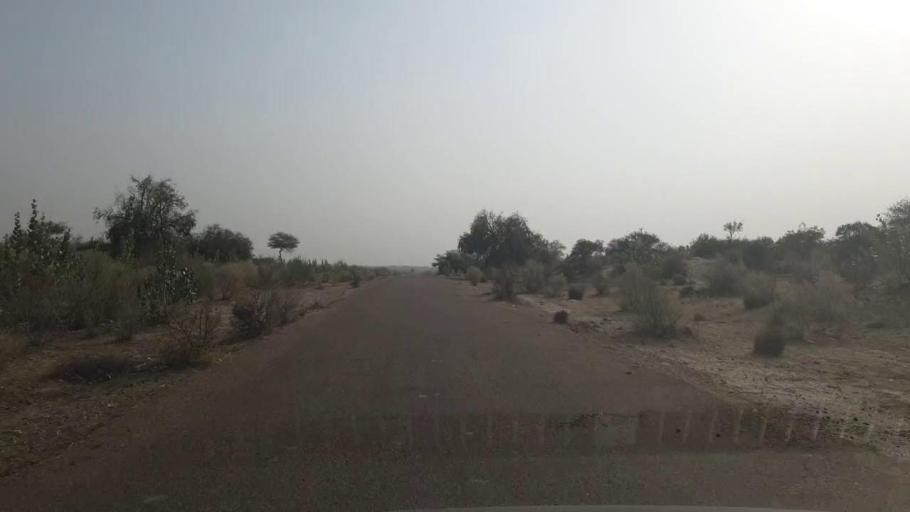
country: PK
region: Sindh
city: Chor
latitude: 25.4795
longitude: 69.9741
